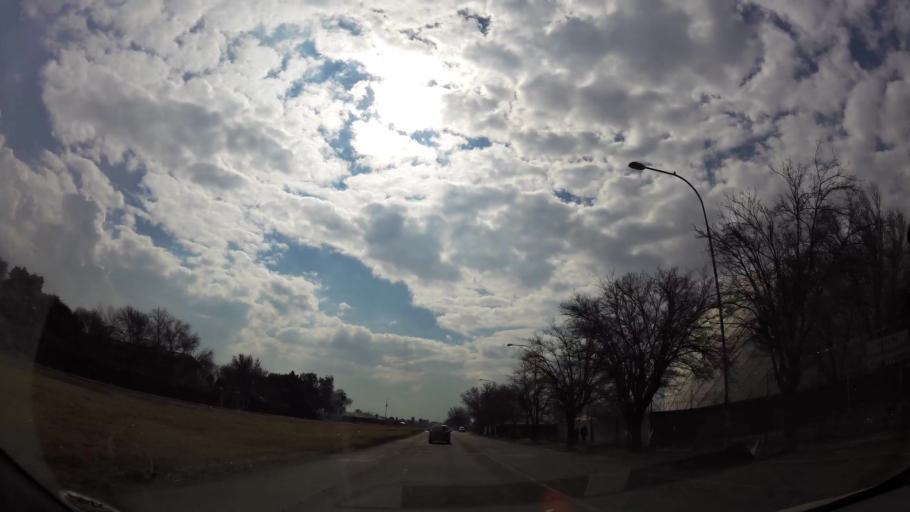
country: ZA
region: Gauteng
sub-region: Sedibeng District Municipality
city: Vereeniging
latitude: -26.6693
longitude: 27.9197
